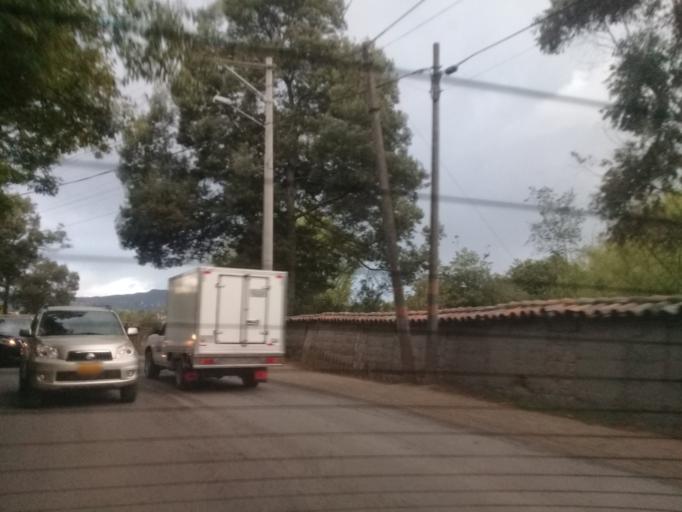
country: CO
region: Cundinamarca
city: Cajica
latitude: 4.9276
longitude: -74.0503
